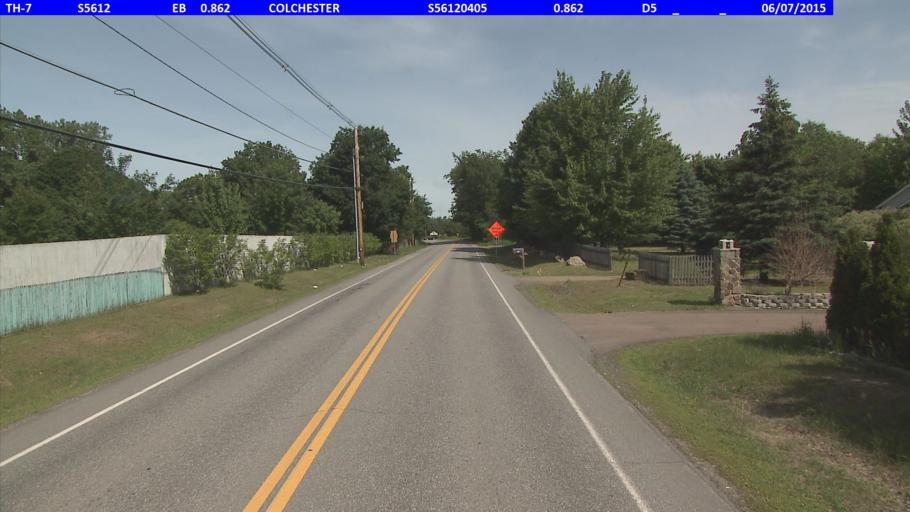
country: US
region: Vermont
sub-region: Chittenden County
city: Colchester
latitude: 44.5218
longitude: -73.1518
